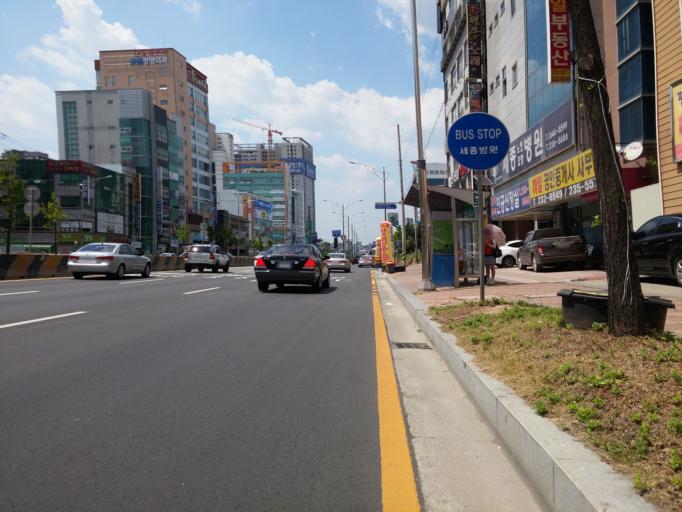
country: KR
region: Chungcheongbuk-do
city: Cheongju-si
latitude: 36.6234
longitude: 127.4324
